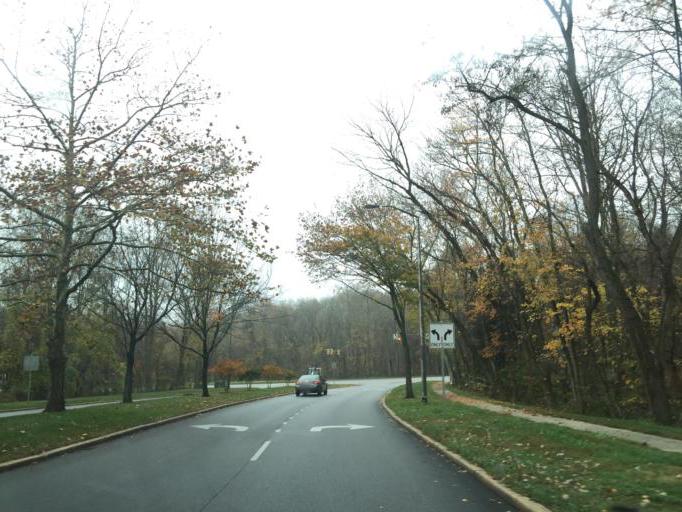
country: US
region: Maryland
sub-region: Howard County
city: Riverside
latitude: 39.1918
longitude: -76.8503
